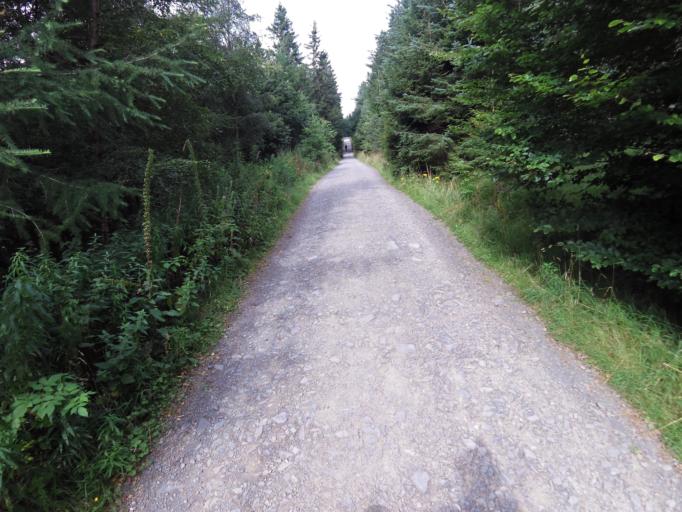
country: GB
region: Scotland
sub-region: The Scottish Borders
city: Peebles
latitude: 55.6592
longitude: -3.1511
